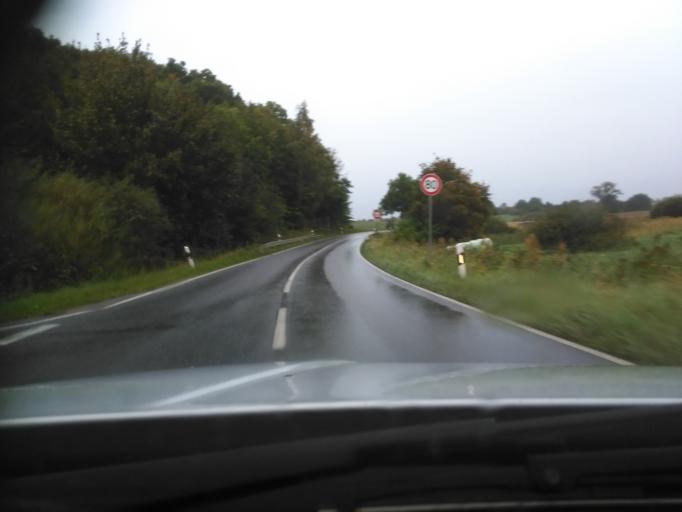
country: DE
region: Mecklenburg-Vorpommern
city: Rambin
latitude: 54.3007
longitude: 13.2047
